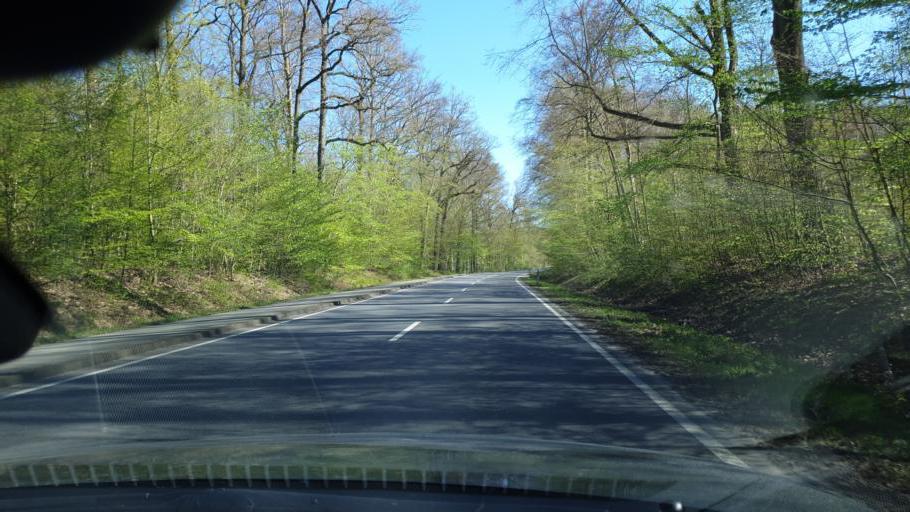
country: DE
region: Mecklenburg-Vorpommern
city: Werdervorstadt
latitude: 53.6576
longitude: 11.4410
